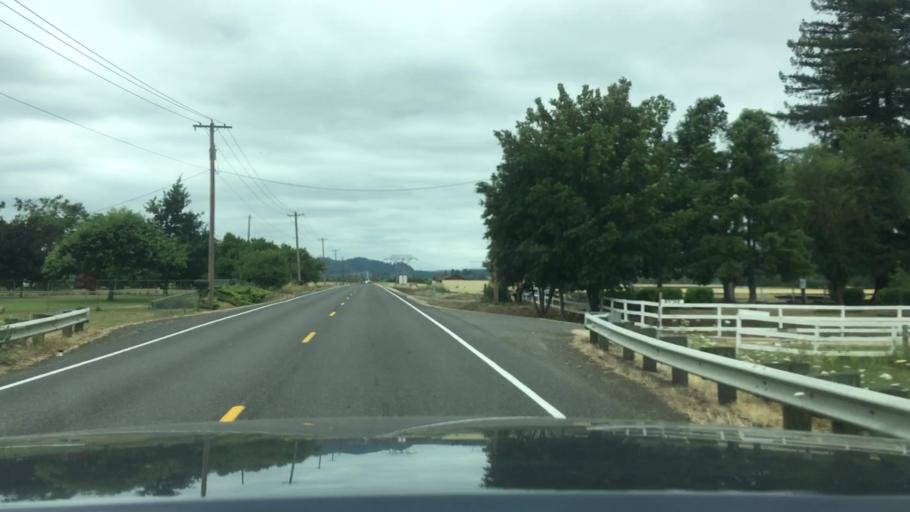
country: US
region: Oregon
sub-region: Lane County
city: Junction City
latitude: 44.0986
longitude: -123.2084
